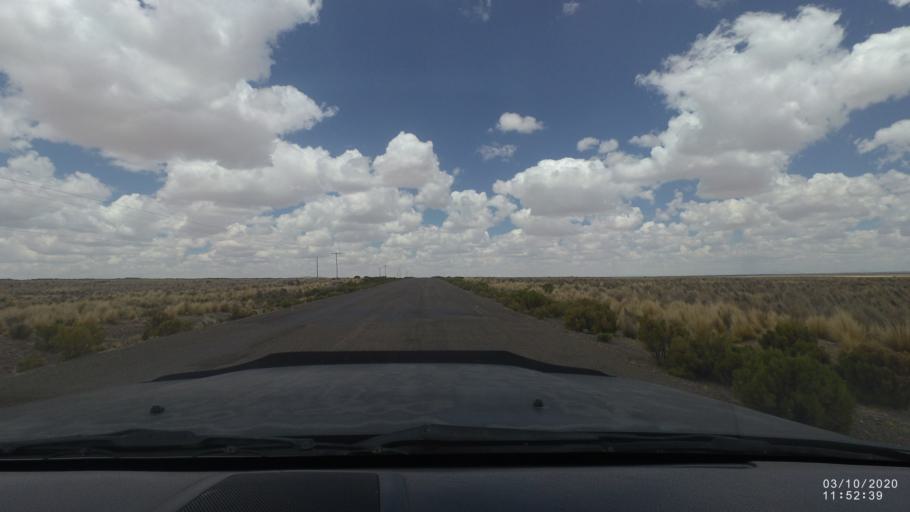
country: BO
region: Oruro
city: Poopo
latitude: -18.4644
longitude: -67.6006
